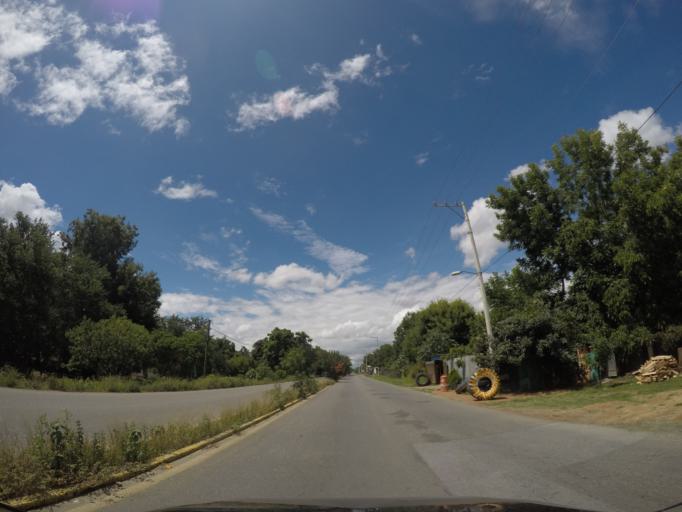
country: MX
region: Oaxaca
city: San Raymundo Jalpam
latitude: 16.9718
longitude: -96.7507
